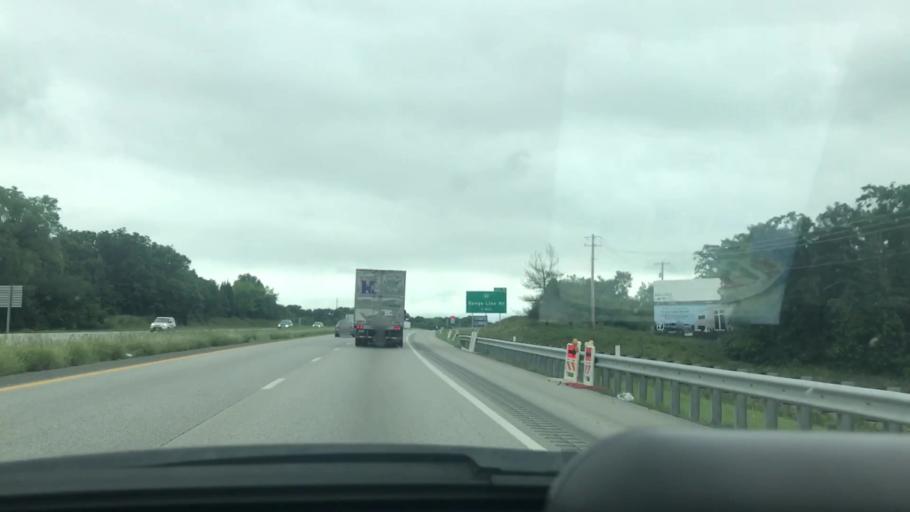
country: US
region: Missouri
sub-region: Jasper County
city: Joplin
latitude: 37.0439
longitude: -94.5026
